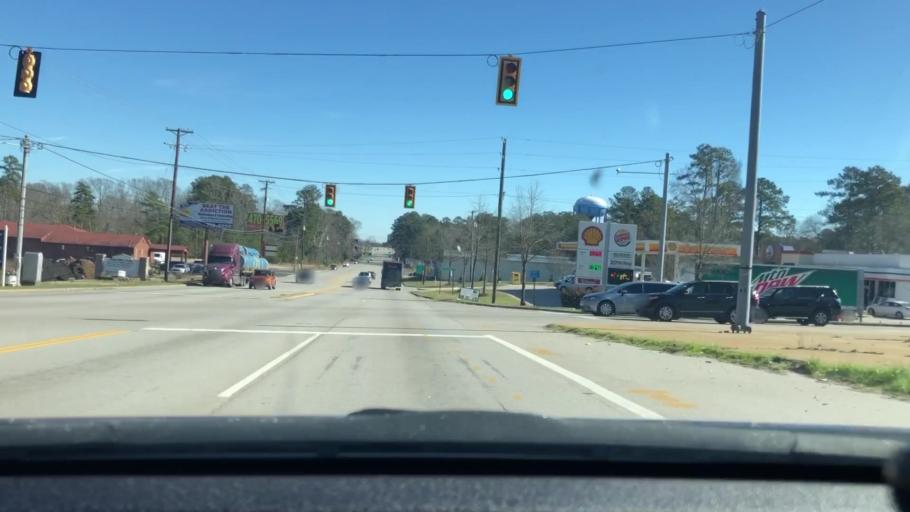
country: US
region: South Carolina
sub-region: Lexington County
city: Oak Grove
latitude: 34.0078
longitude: -81.1422
